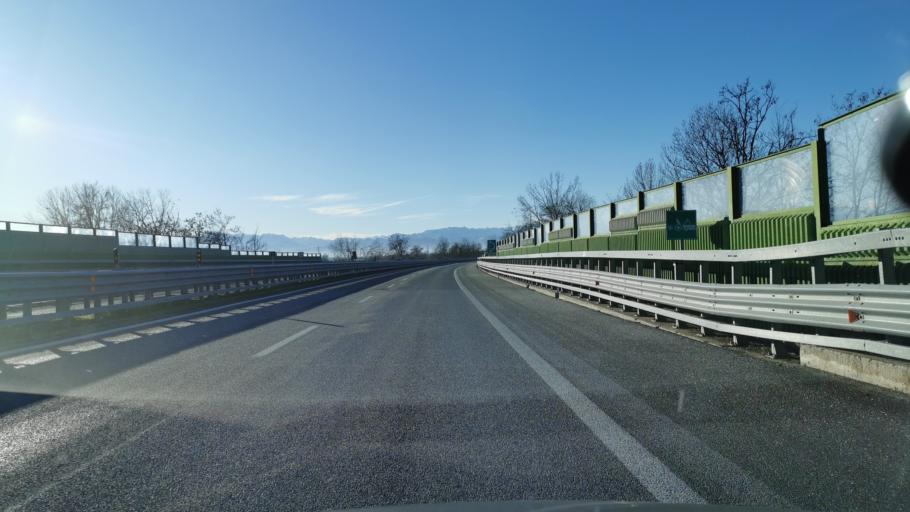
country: IT
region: Piedmont
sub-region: Provincia di Cuneo
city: Magliano Alpi
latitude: 44.4690
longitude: 7.7773
